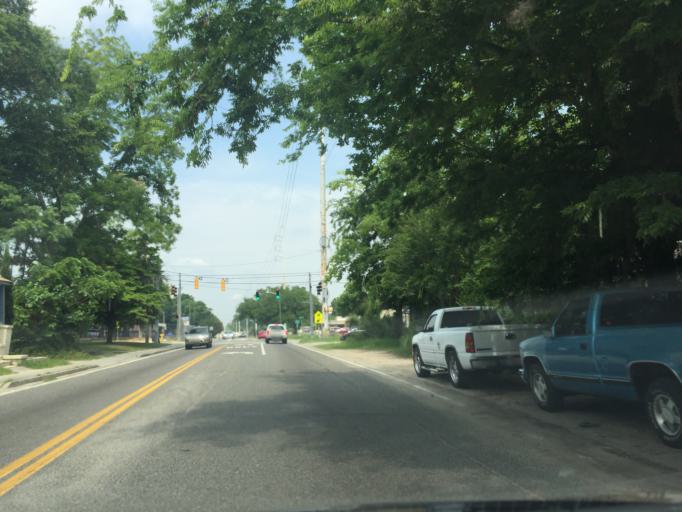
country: US
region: Georgia
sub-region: Chatham County
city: Savannah
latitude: 32.0489
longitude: -81.1164
